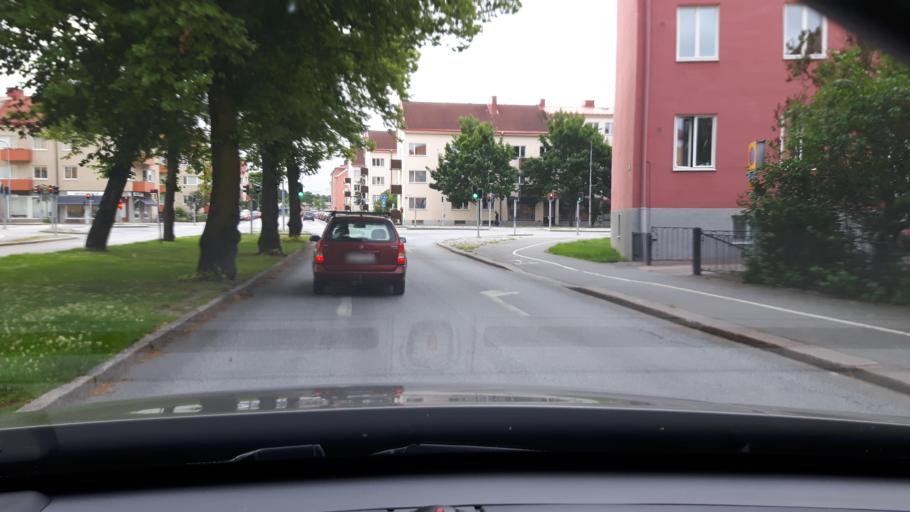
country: SE
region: Uppsala
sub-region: Uppsala Kommun
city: Uppsala
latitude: 59.8585
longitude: 17.6542
